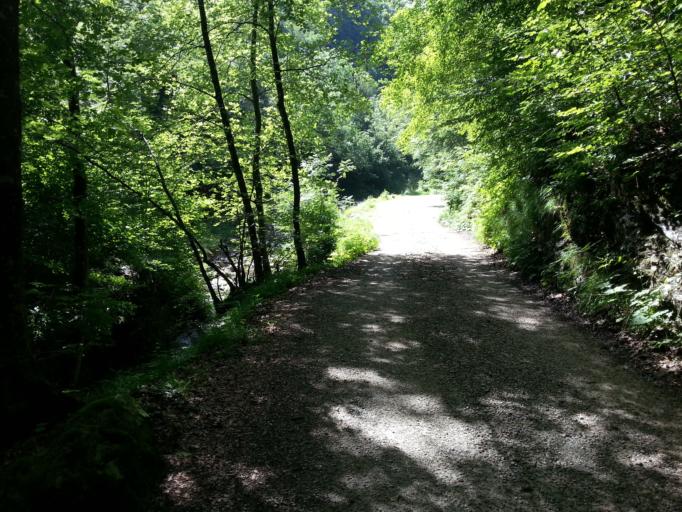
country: IT
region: Lombardy
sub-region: Provincia di Lecco
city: Cremeno
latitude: 45.9196
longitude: 9.4594
